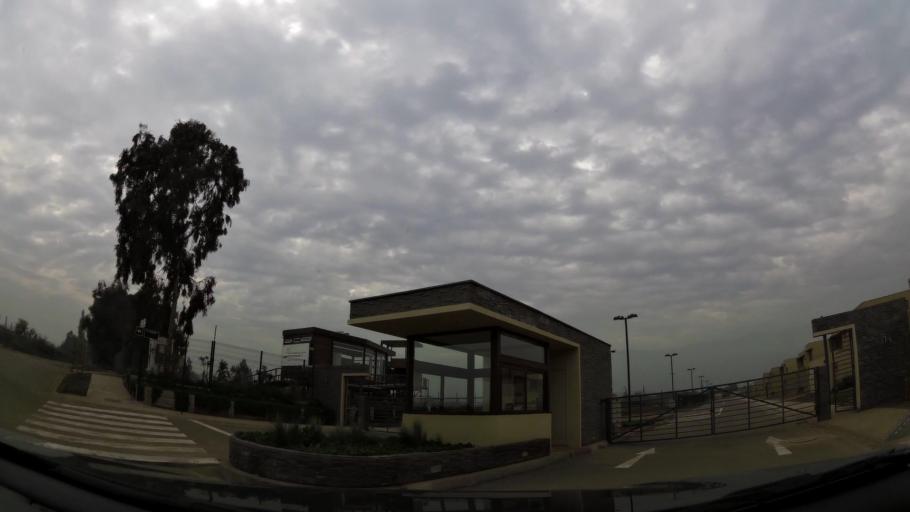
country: CL
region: Santiago Metropolitan
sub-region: Provincia de Chacabuco
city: Chicureo Abajo
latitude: -33.2270
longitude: -70.6718
